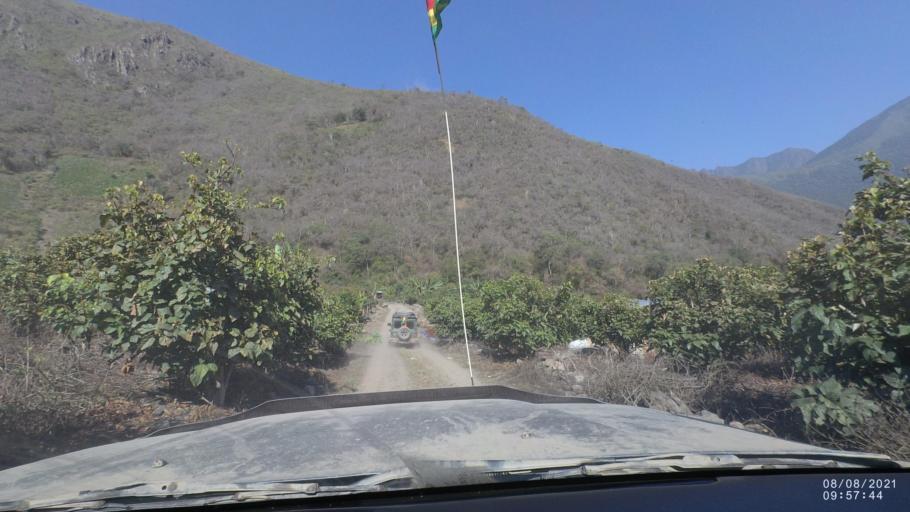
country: BO
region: La Paz
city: Quime
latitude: -16.6422
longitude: -66.7257
